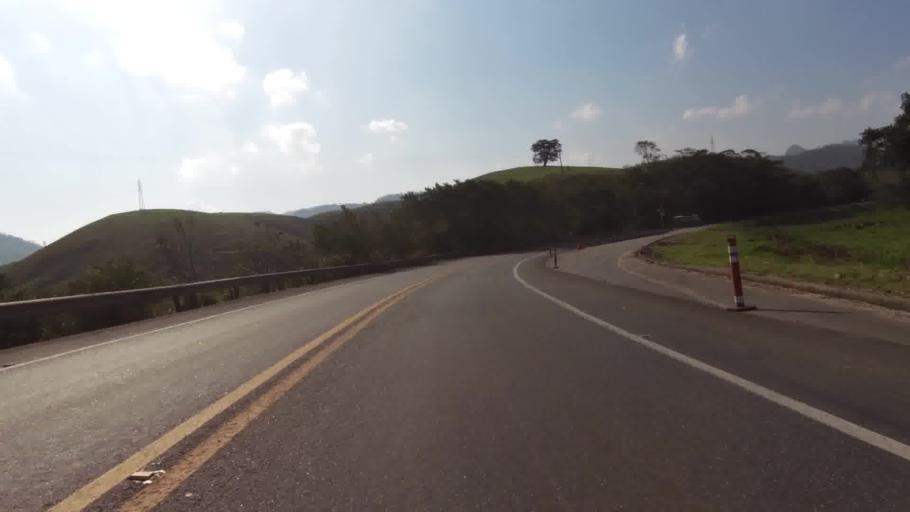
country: BR
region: Espirito Santo
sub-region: Rio Novo Do Sul
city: Rio Novo do Sul
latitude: -20.8554
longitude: -40.8783
